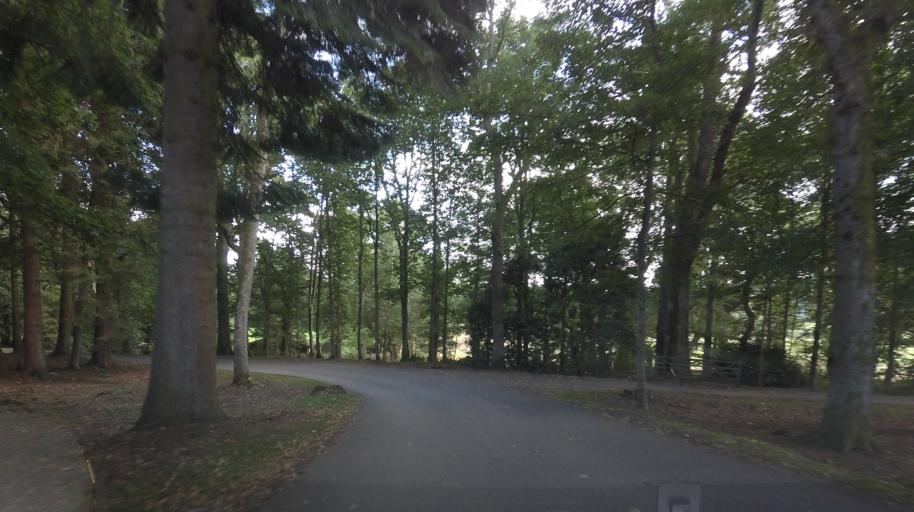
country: GB
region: Scotland
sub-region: Aberdeenshire
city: Banchory
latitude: 57.0600
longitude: -2.4383
